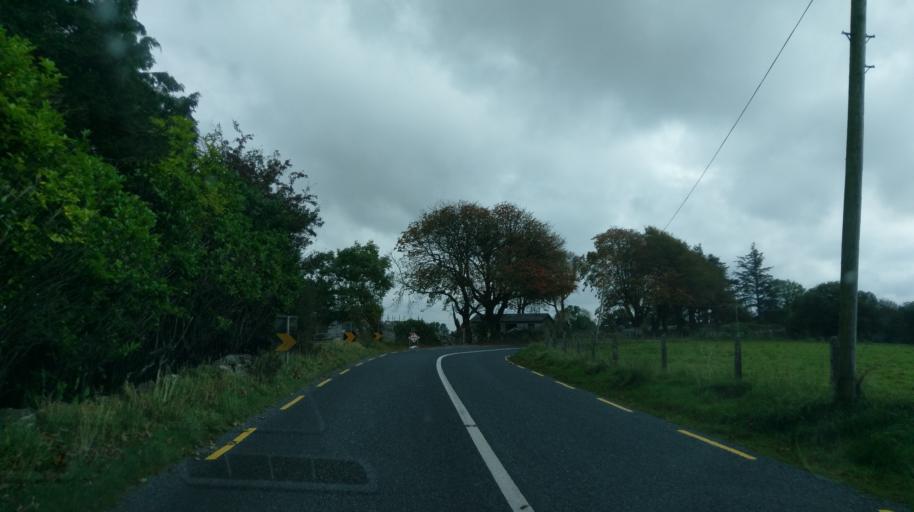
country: IE
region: Connaught
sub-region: County Galway
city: Ballinasloe
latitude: 53.4438
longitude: -8.4612
